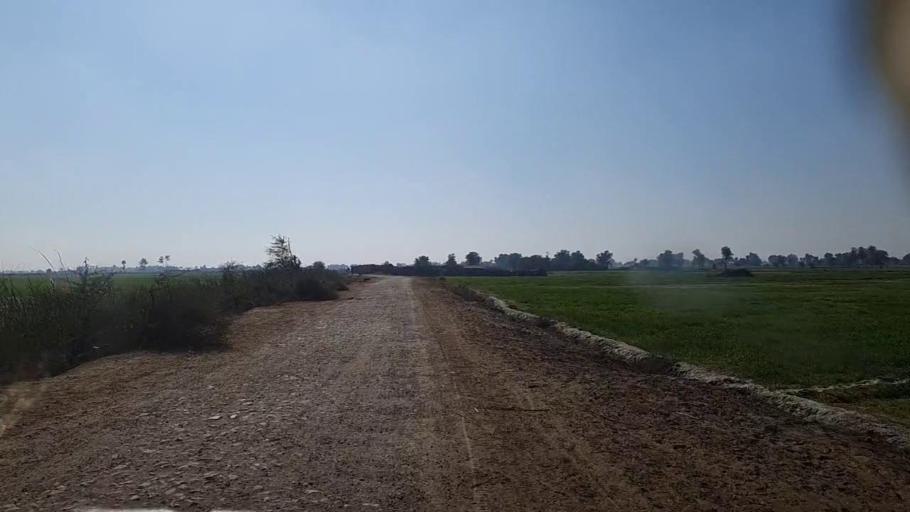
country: PK
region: Sindh
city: Khairpur
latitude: 28.0397
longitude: 69.7826
